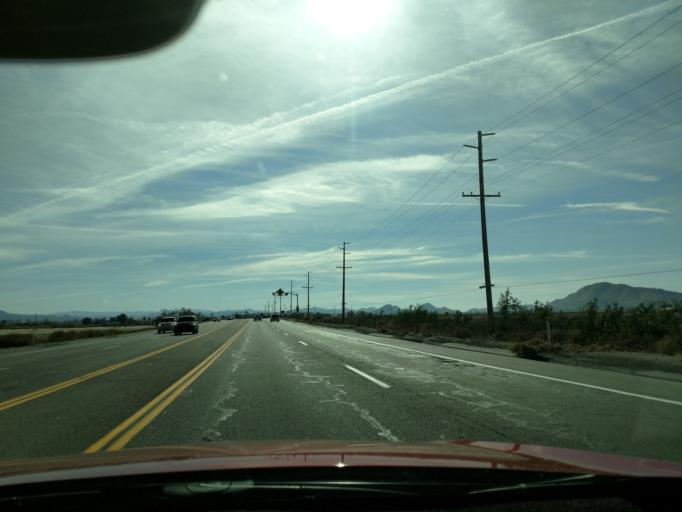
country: US
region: California
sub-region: Riverside County
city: San Jacinto
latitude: 33.8277
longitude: -117.0036
